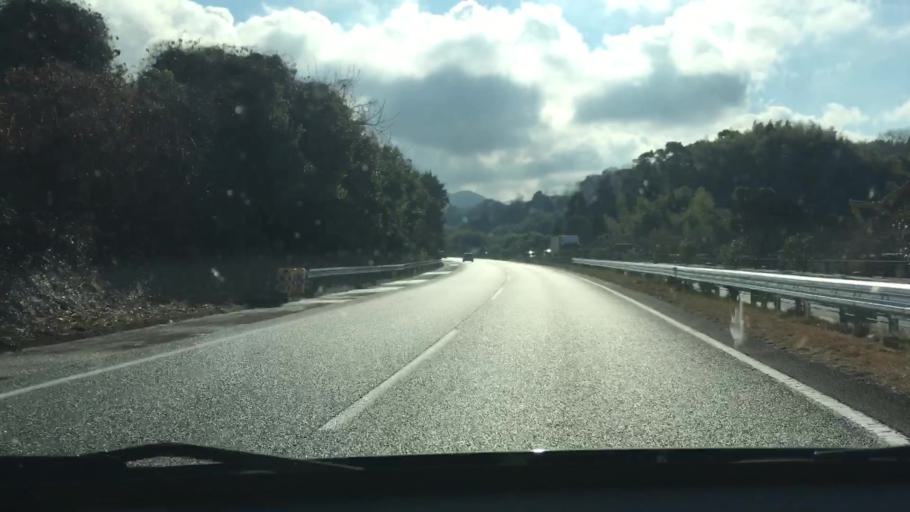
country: JP
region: Kumamoto
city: Matsubase
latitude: 32.5601
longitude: 130.6970
